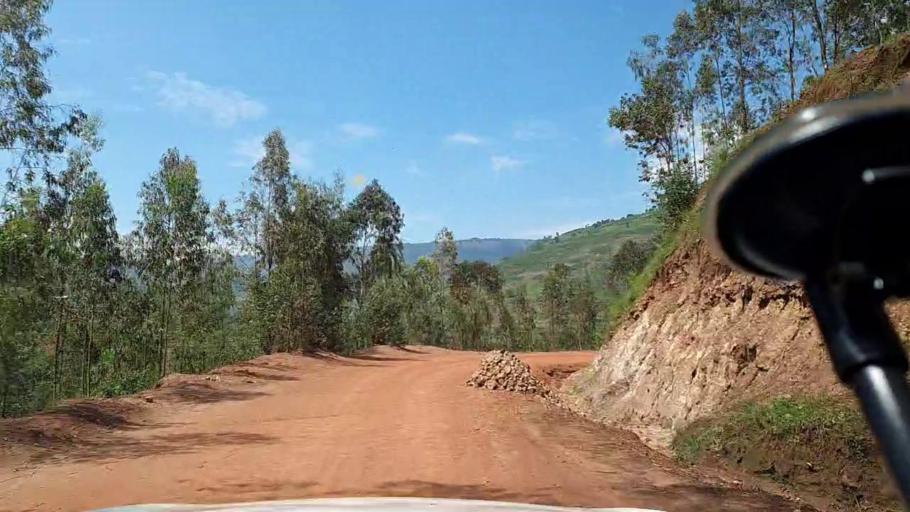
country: RW
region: Kigali
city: Kigali
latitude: -1.7999
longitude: 29.8878
